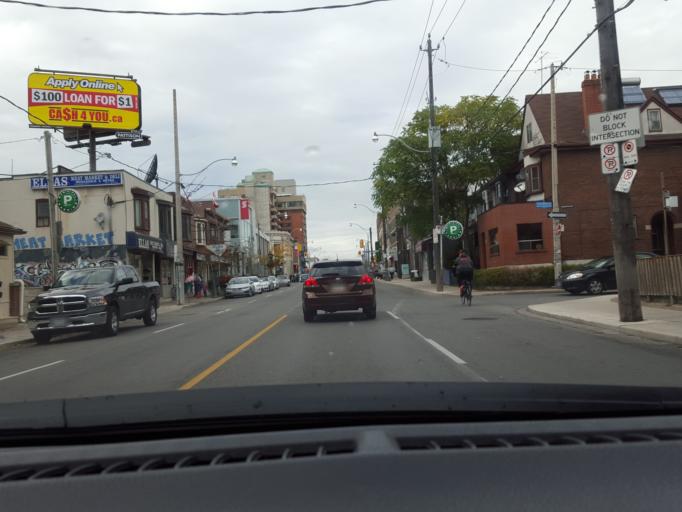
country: CA
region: Ontario
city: Toronto
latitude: 43.6779
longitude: -79.3445
